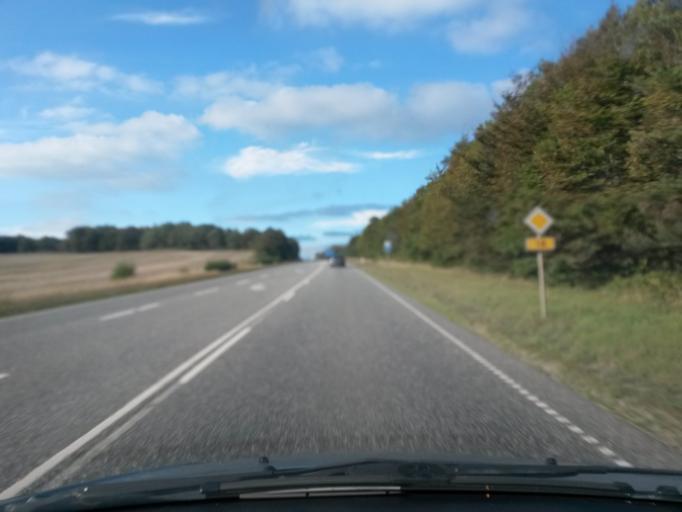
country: DK
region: Central Jutland
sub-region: Herning Kommune
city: Avlum
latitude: 56.2827
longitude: 8.7490
